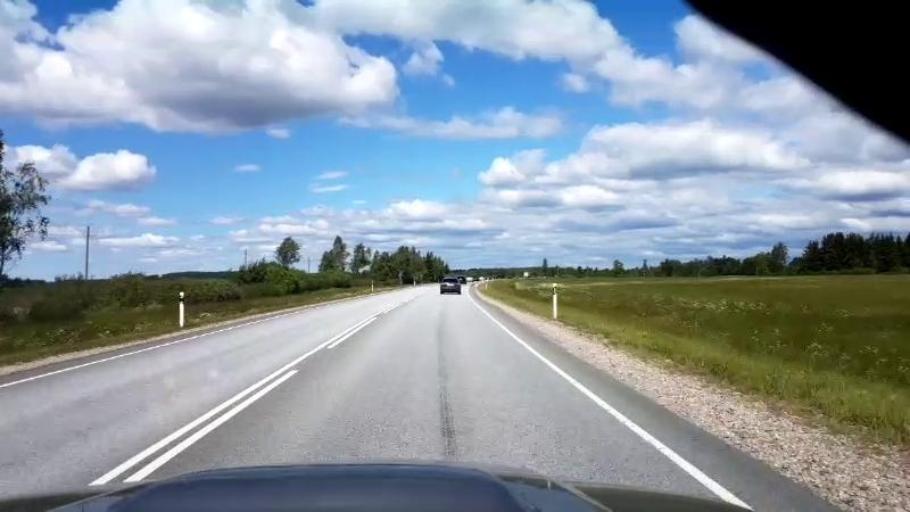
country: EE
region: Paernumaa
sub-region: Sauga vald
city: Sauga
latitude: 58.4882
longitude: 24.5287
